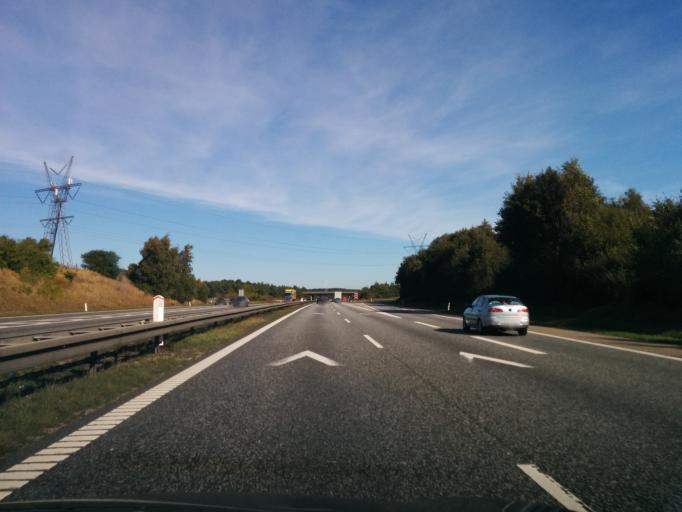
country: DK
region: Central Jutland
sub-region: Horsens Kommune
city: Horsens
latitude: 55.8823
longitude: 9.7860
